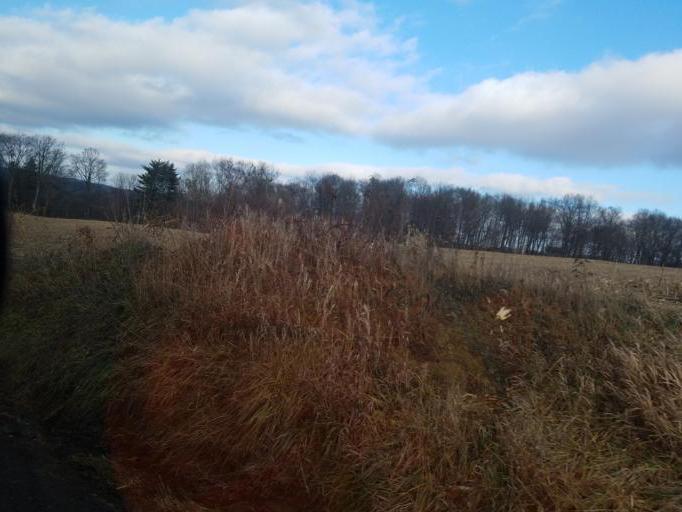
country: US
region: Ohio
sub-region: Ashland County
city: Loudonville
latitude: 40.6297
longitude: -82.3673
